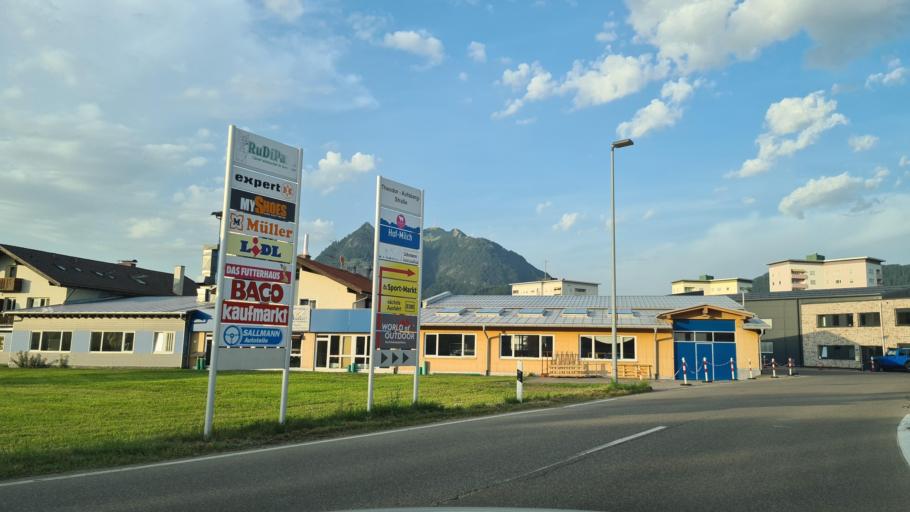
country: DE
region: Bavaria
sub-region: Swabia
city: Sonthofen
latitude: 47.5164
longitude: 10.2706
